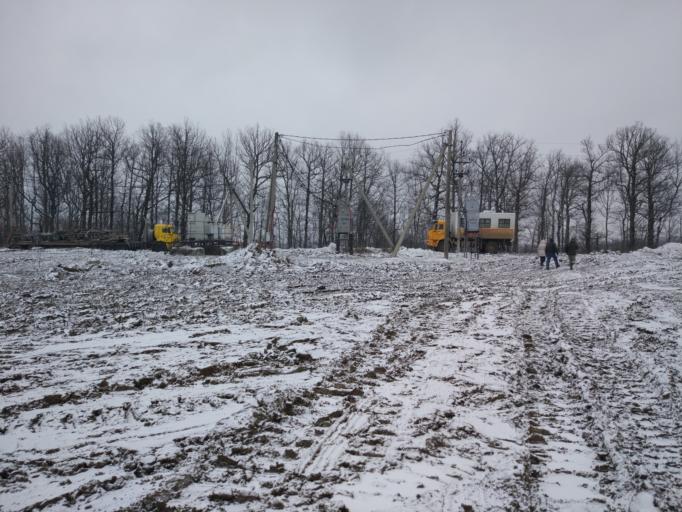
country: RU
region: Krasnodarskiy
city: Saratovskaya
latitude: 44.6175
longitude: 39.2358
